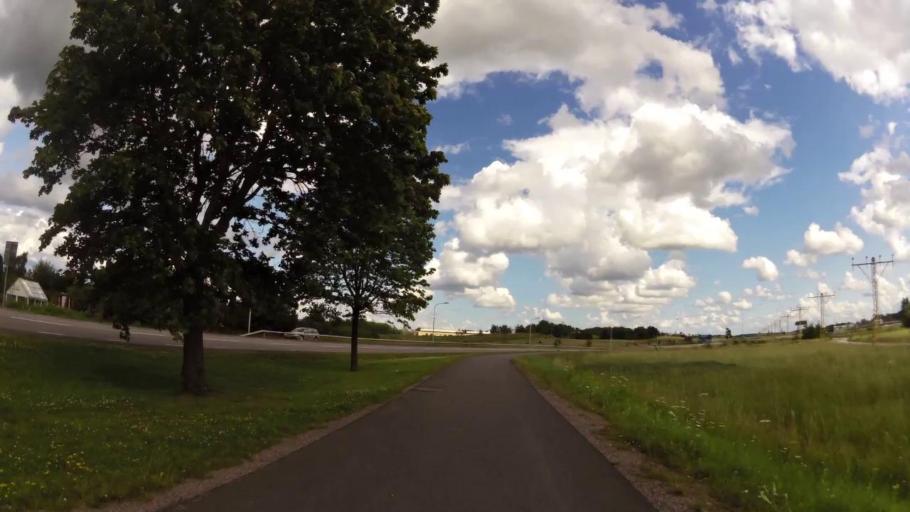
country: SE
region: OEstergoetland
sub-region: Linkopings Kommun
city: Linkoping
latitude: 58.4129
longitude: 15.6499
